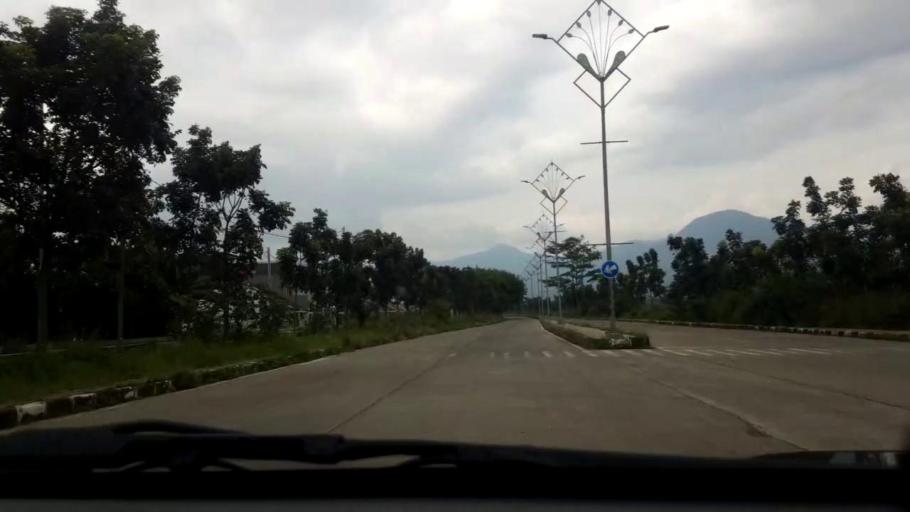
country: ID
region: West Java
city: Cileunyi
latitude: -6.9545
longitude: 107.7108
